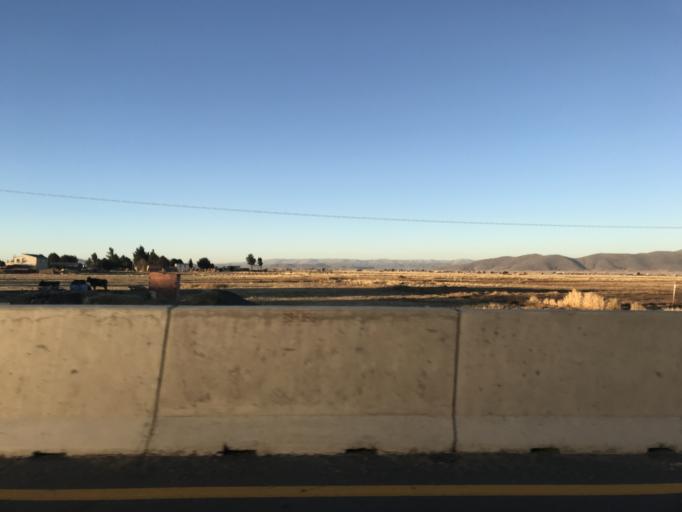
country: BO
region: La Paz
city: Batallas
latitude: -16.2994
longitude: -68.4979
